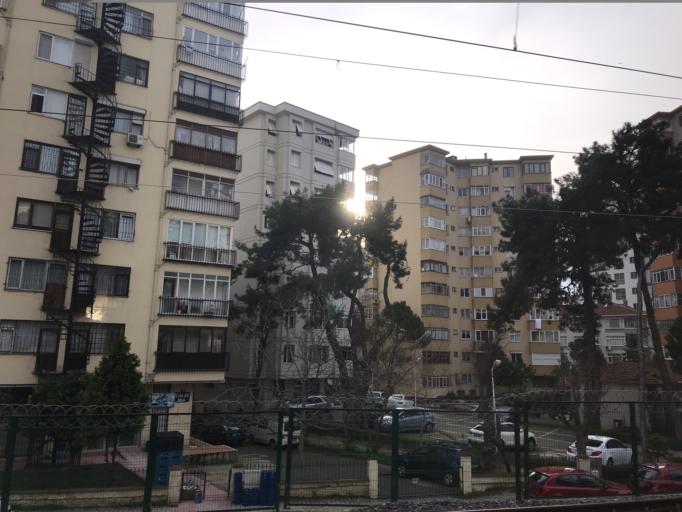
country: TR
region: Istanbul
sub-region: Atasehir
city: Atasehir
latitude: 40.9677
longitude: 29.0783
